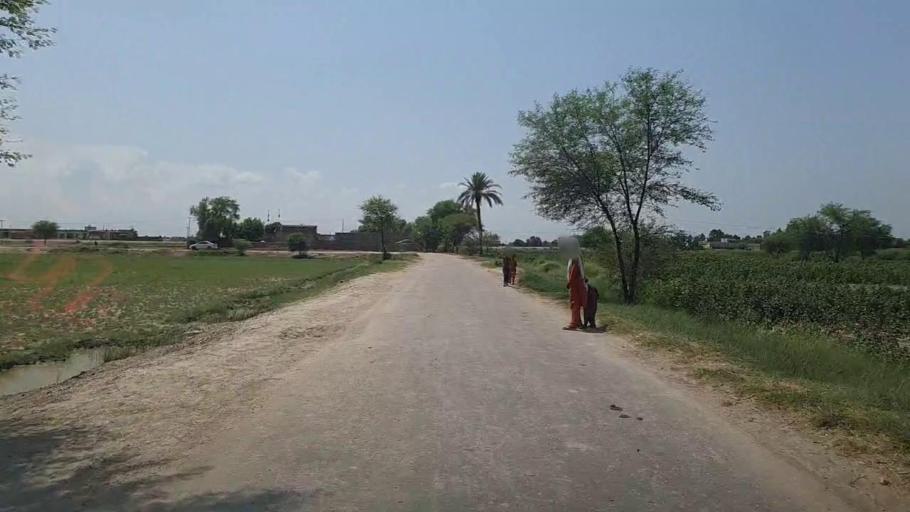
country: PK
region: Sindh
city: Ubauro
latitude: 28.1857
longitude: 69.7999
